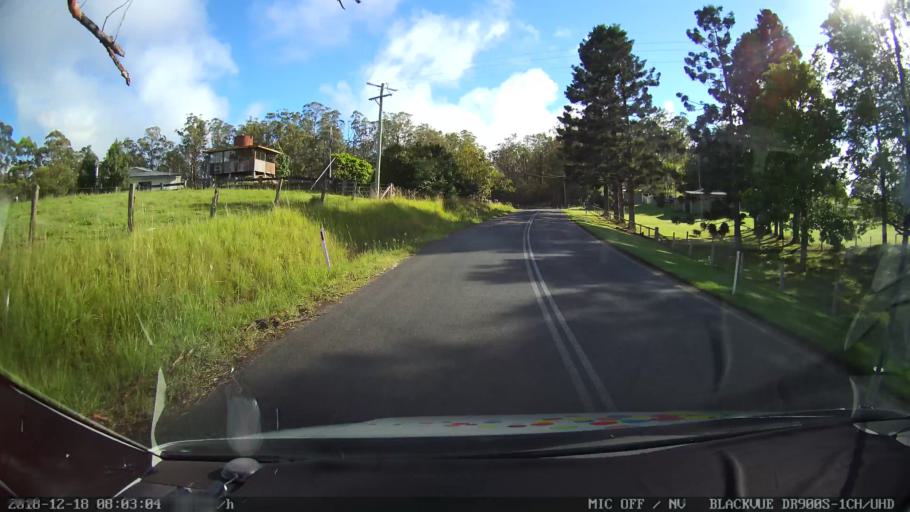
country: AU
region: New South Wales
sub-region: Kyogle
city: Kyogle
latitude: -28.3882
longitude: 152.6376
